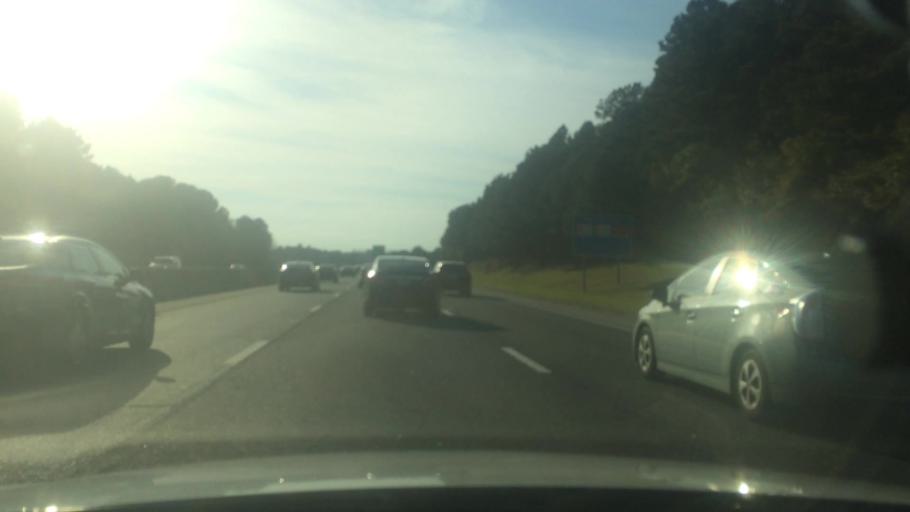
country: US
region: North Carolina
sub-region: Durham County
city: Durham
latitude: 35.9056
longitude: -78.9525
